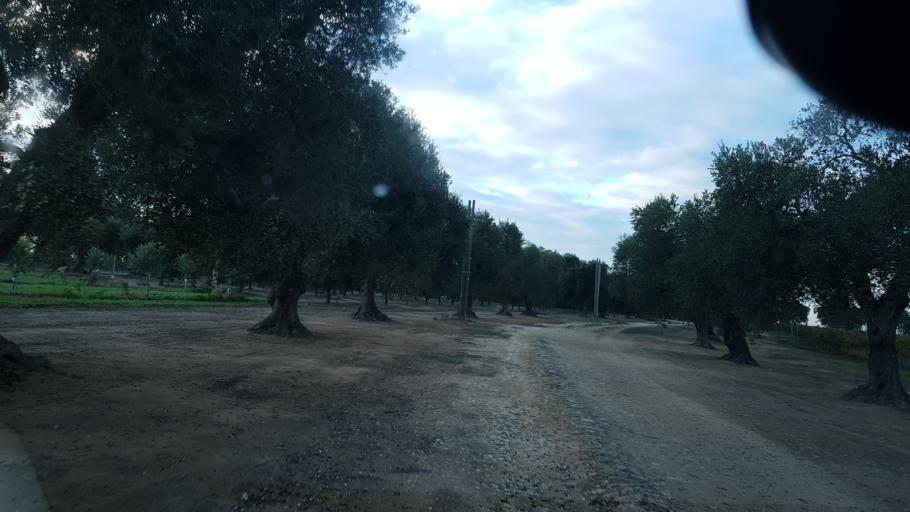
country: IT
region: Apulia
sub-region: Provincia di Brindisi
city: La Rosa
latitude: 40.5878
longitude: 17.9918
